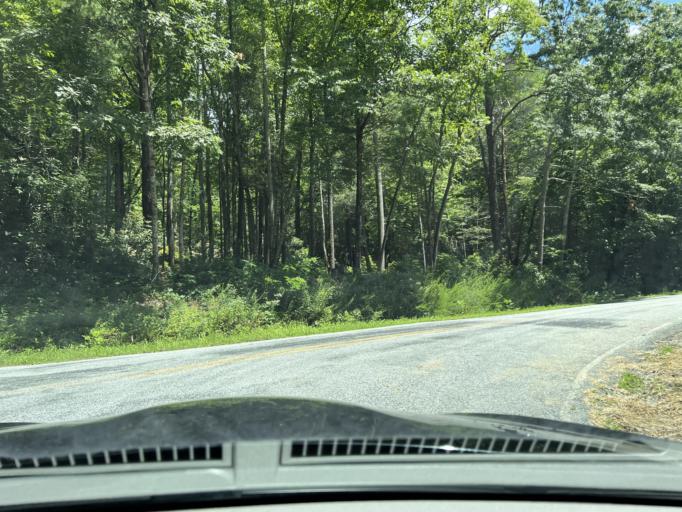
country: US
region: North Carolina
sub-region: Henderson County
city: Fruitland
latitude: 35.4185
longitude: -82.4054
